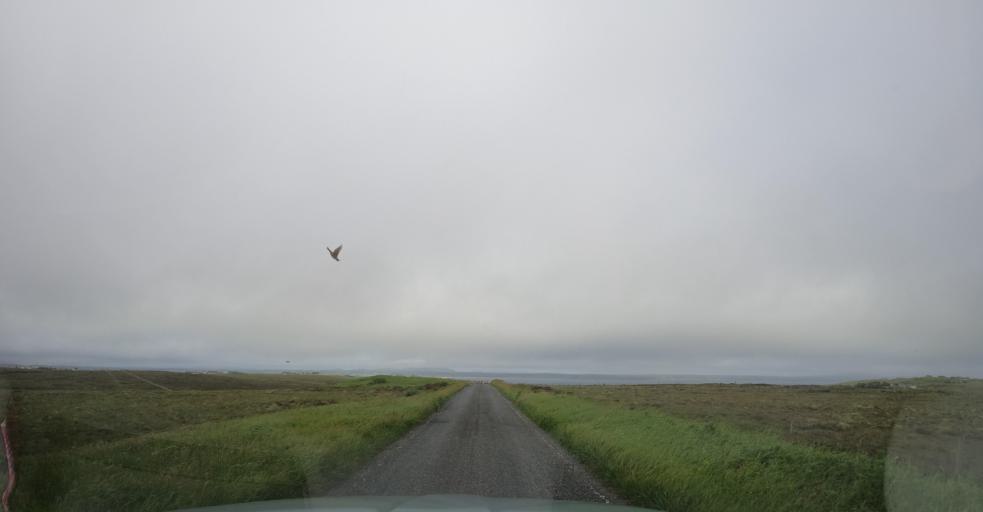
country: GB
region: Scotland
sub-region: Eilean Siar
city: Stornoway
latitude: 58.2039
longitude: -6.2434
